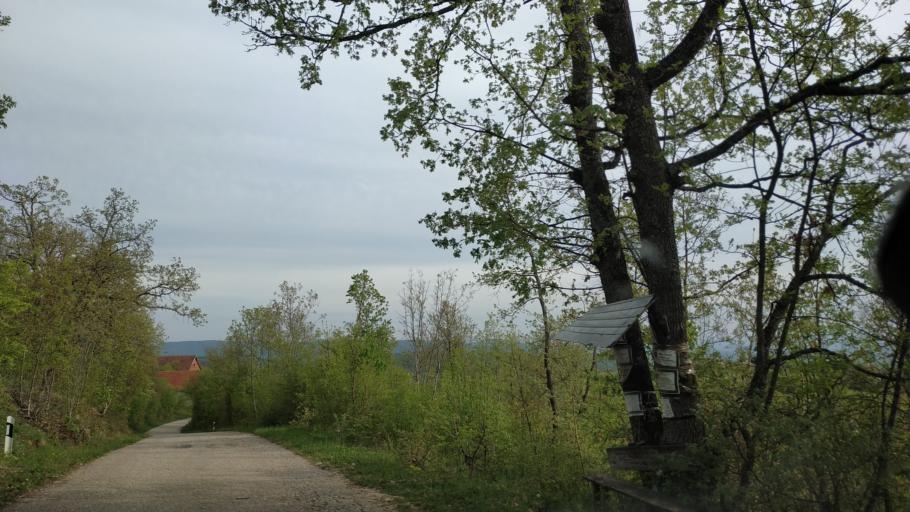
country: RS
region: Central Serbia
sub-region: Zajecarski Okrug
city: Soko Banja
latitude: 43.5401
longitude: 21.8789
